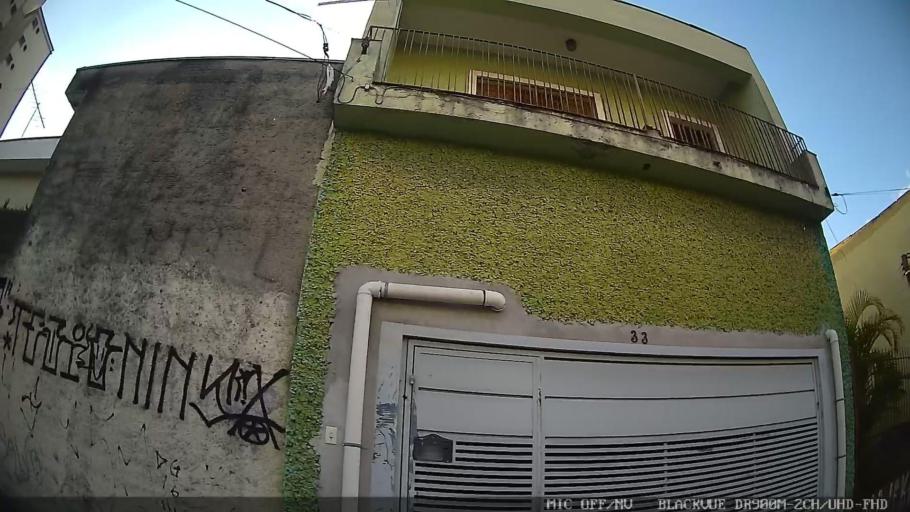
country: BR
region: Sao Paulo
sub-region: Sao Caetano Do Sul
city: Sao Caetano do Sul
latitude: -23.5845
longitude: -46.5394
